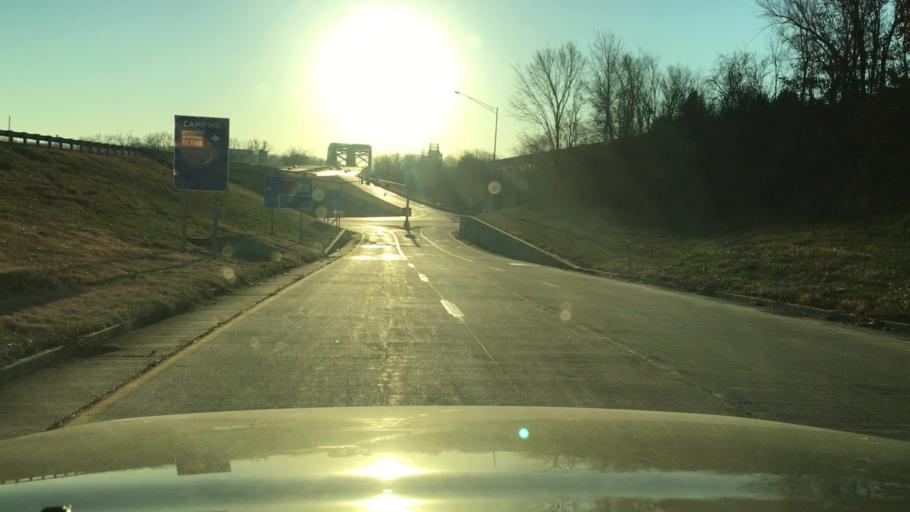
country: US
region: Missouri
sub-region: Saint Charles County
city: Saint Charles
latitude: 38.8035
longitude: -90.4766
